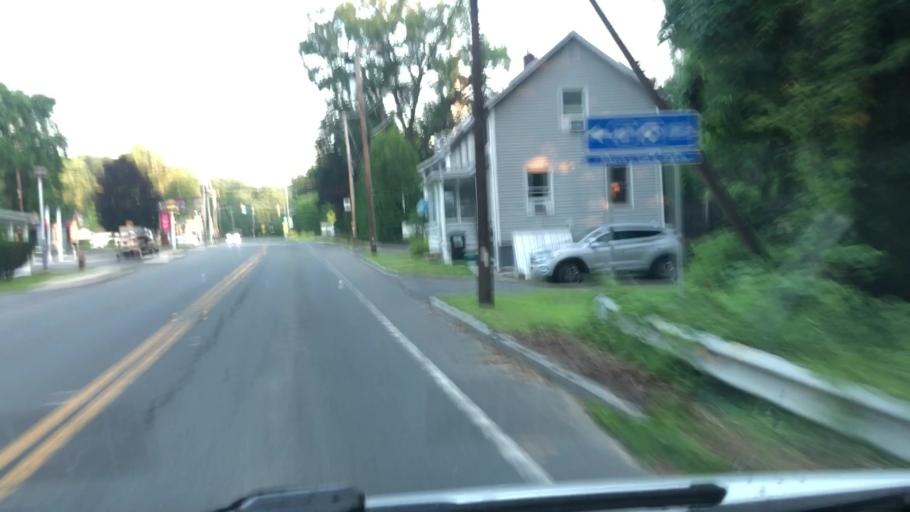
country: US
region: Massachusetts
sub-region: Hampshire County
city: Williamsburg
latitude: 42.3739
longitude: -72.7010
